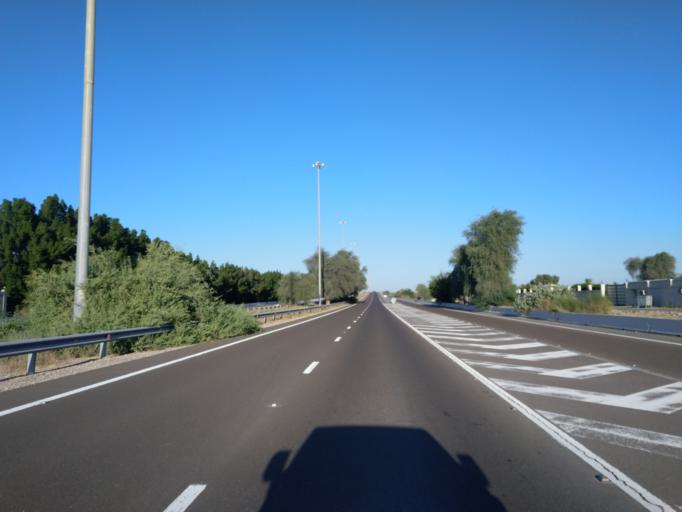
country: OM
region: Al Buraimi
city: Al Buraymi
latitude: 24.5485
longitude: 55.6720
